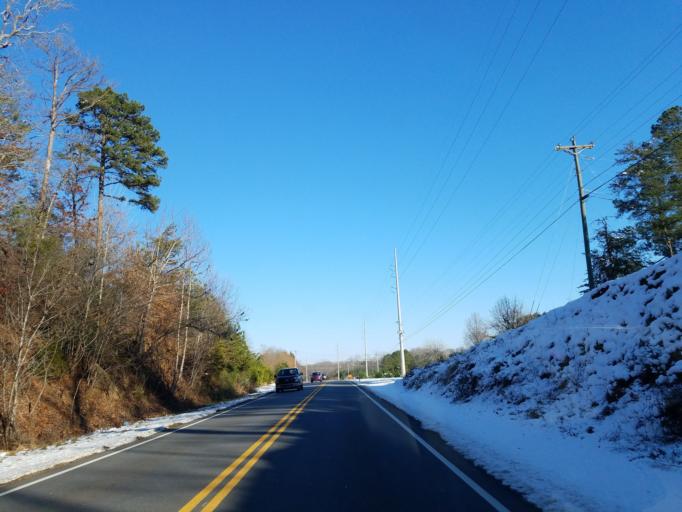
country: US
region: Georgia
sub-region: Dawson County
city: Dawsonville
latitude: 34.3535
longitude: -84.0680
